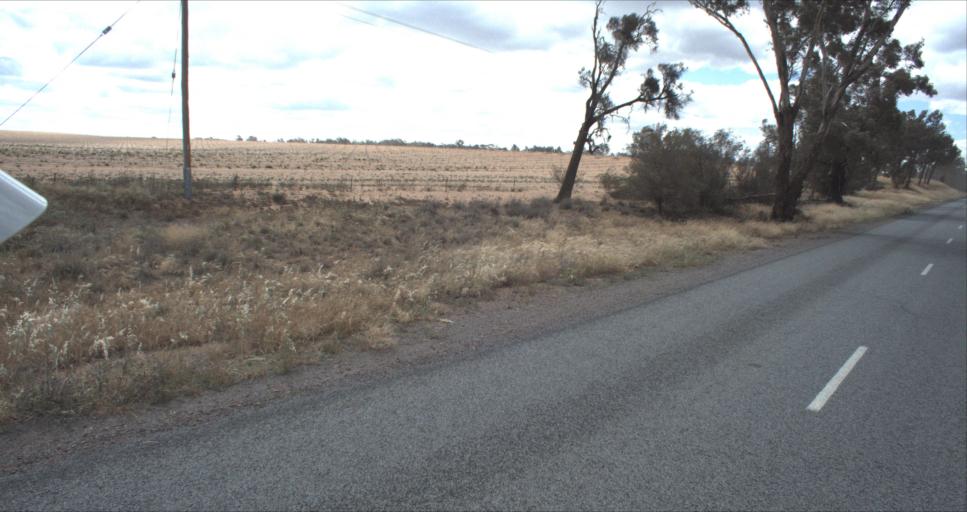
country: AU
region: New South Wales
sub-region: Leeton
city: Leeton
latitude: -34.6616
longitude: 146.3492
